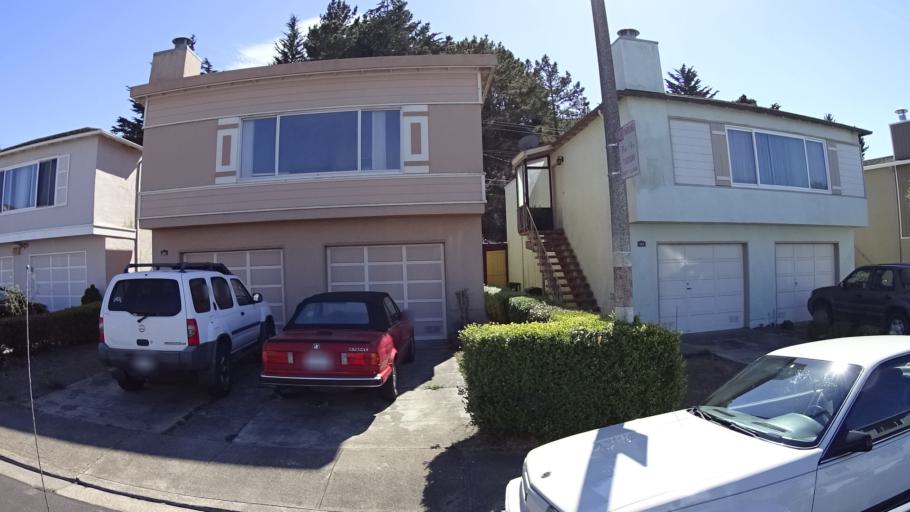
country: US
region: California
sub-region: San Mateo County
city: Daly City
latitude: 37.7044
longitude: -122.4384
